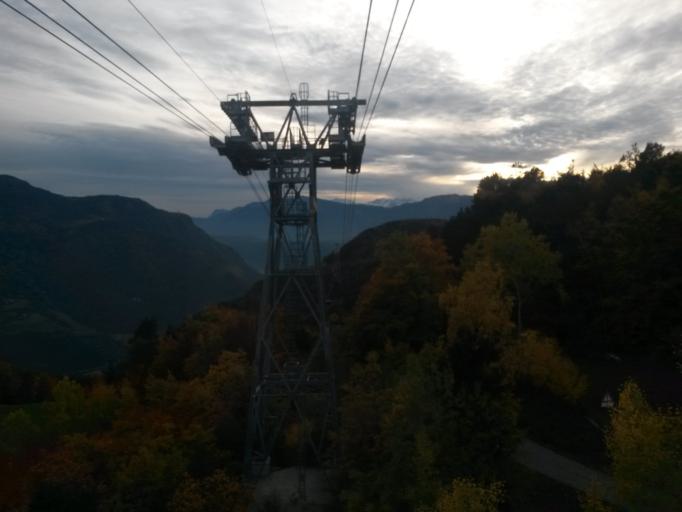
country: IT
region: Trentino-Alto Adige
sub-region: Bolzano
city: Soprabolzano
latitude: 46.5219
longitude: 11.3963
